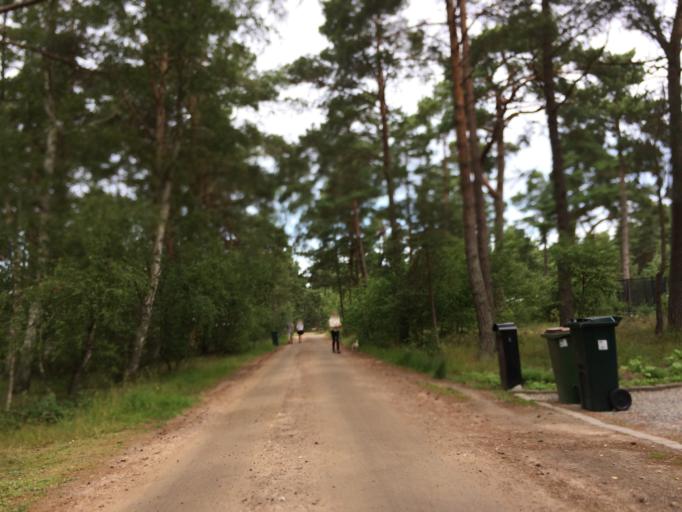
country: SE
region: Skane
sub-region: Vellinge Kommun
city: Ljunghusen
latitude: 55.3999
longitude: 12.9291
